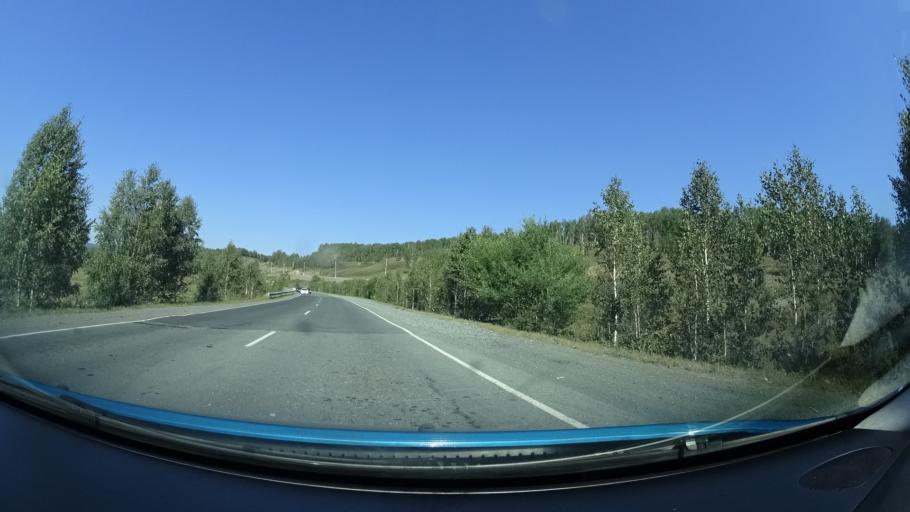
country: RU
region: Bashkortostan
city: Abzakovo
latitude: 53.8209
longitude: 58.6376
